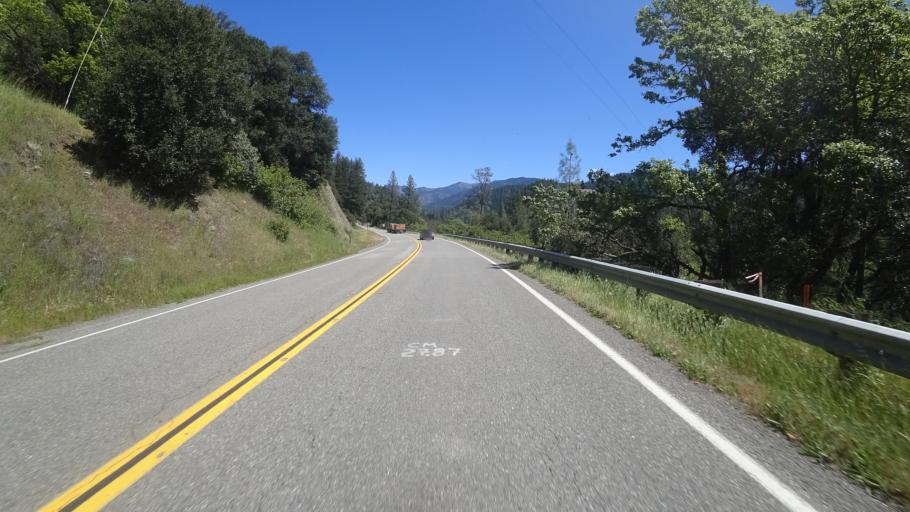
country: US
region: California
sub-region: Trinity County
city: Hayfork
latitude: 40.7419
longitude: -123.2652
